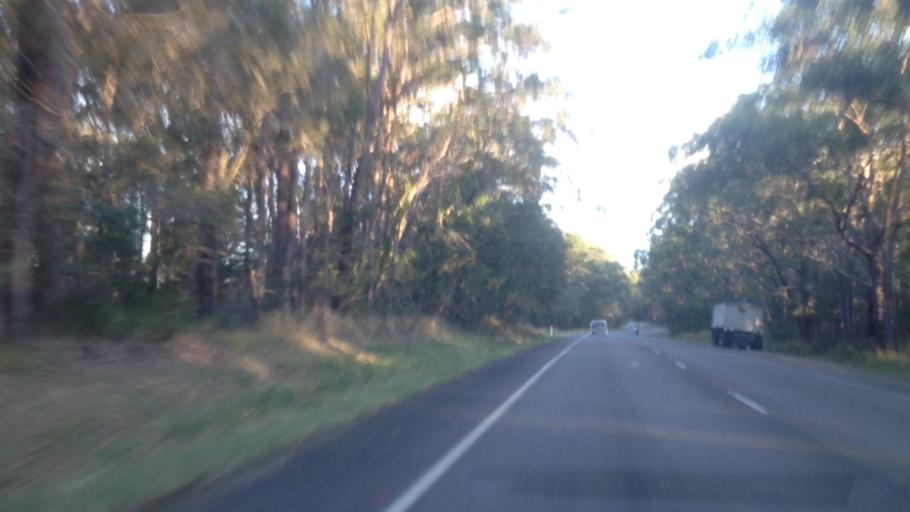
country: AU
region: New South Wales
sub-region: Lake Macquarie Shire
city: Cooranbong
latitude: -33.0543
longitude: 151.4732
